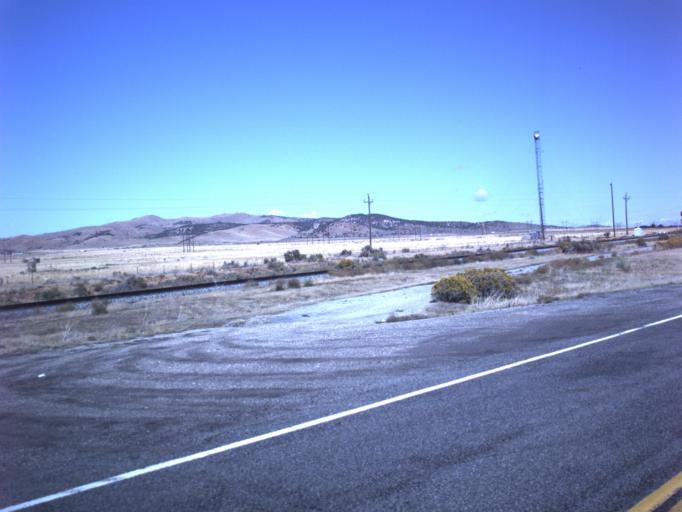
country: US
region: Utah
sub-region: Juab County
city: Nephi
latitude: 39.5553
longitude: -111.9210
